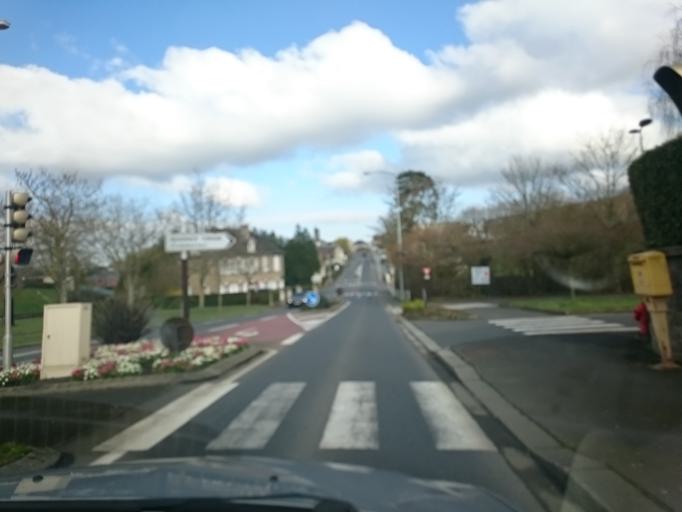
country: FR
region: Lower Normandy
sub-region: Departement de la Manche
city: Saint-Lo
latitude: 49.1126
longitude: -1.0785
